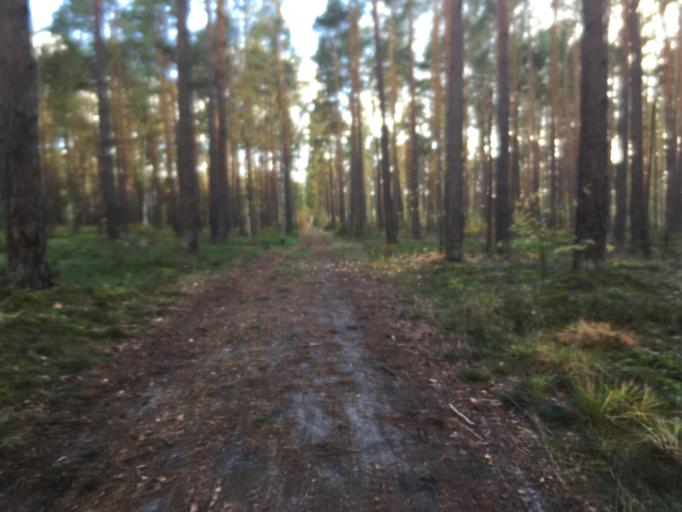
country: DE
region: Brandenburg
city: Birkenwerder
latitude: 52.6957
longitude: 13.3370
